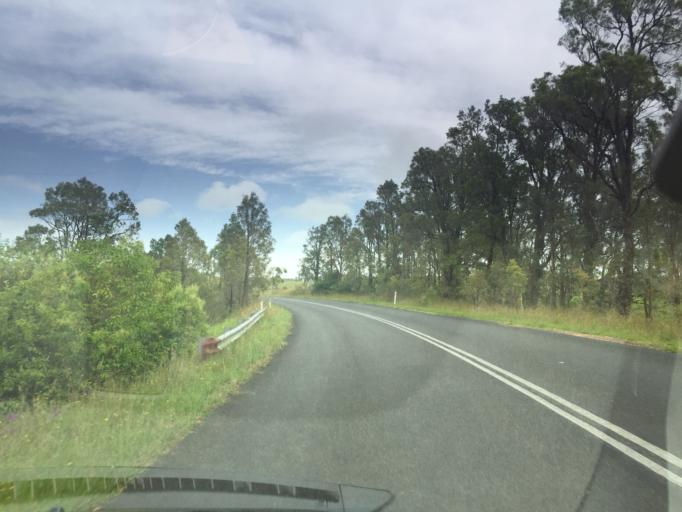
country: AU
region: New South Wales
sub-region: Bega Valley
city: Bega
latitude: -36.6975
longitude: 149.5893
